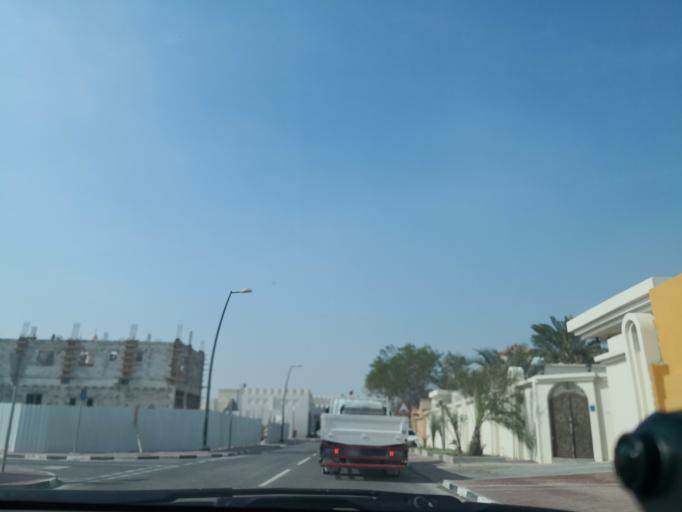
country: QA
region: Baladiyat ad Dawhah
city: Doha
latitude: 25.3466
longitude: 51.4935
